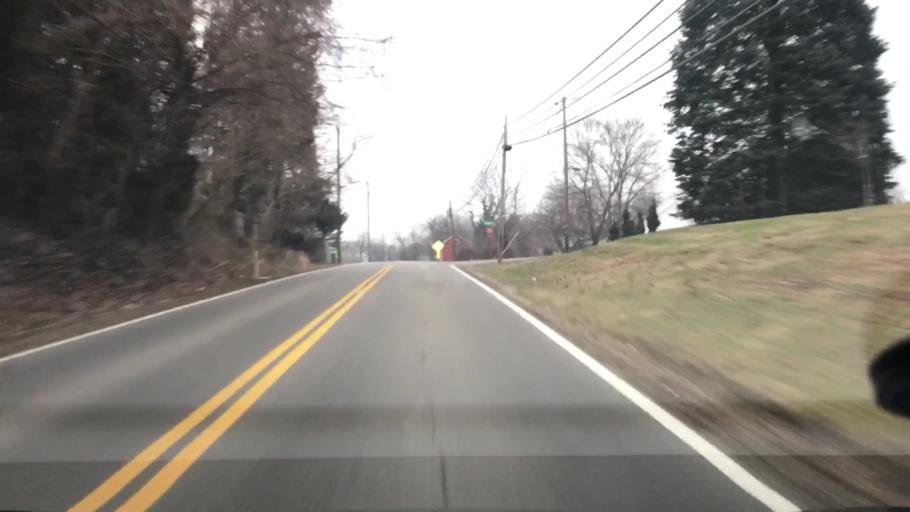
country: US
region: Ohio
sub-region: Clark County
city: Springfield
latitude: 39.8818
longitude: -83.8425
